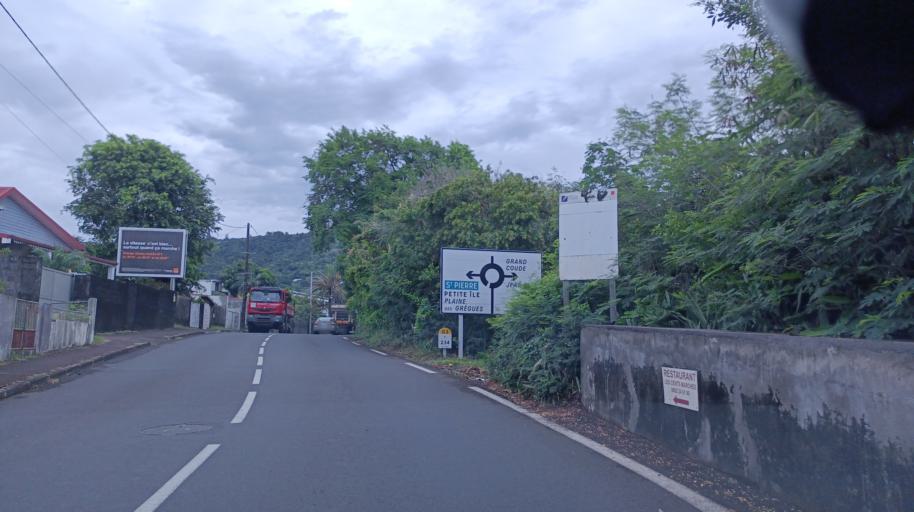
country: RE
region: Reunion
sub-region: Reunion
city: Saint-Joseph
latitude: -21.3751
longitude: 55.6154
